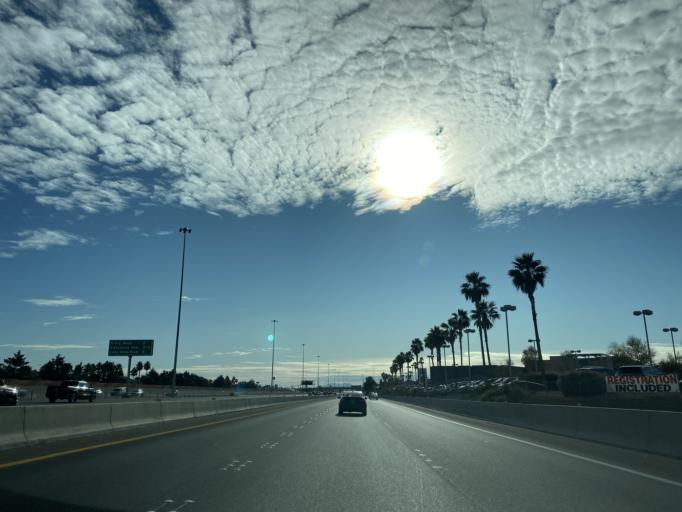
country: US
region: Nevada
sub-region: Clark County
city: Las Vegas
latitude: 36.2700
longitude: -115.2605
